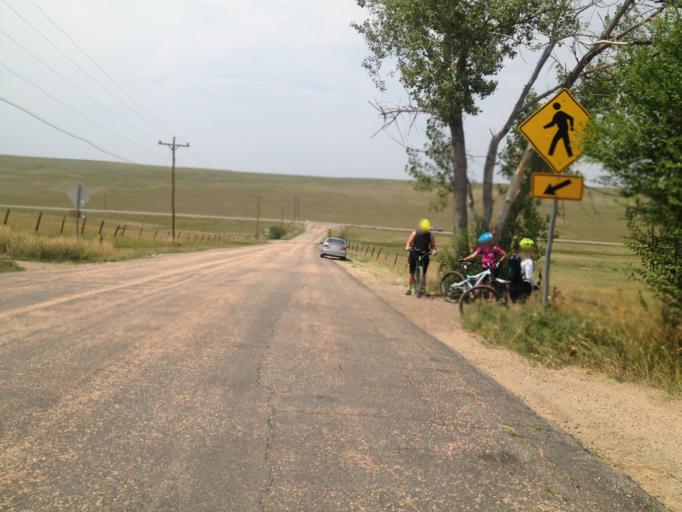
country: US
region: Colorado
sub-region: Boulder County
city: Superior
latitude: 39.9589
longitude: -105.1995
